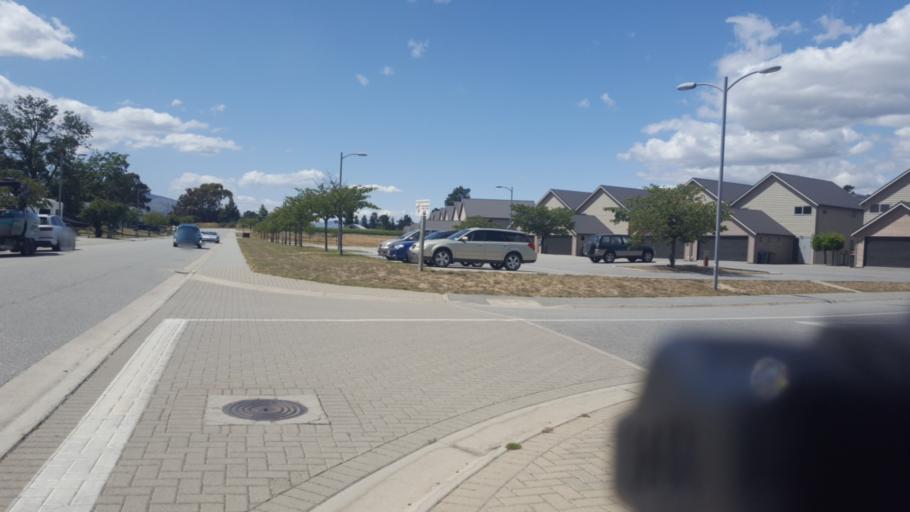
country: NZ
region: Otago
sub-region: Queenstown-Lakes District
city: Wanaka
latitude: -44.9808
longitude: 169.2353
